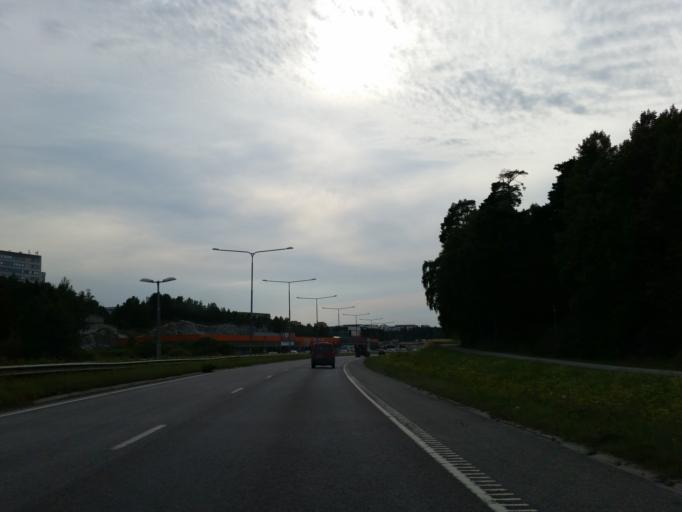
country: SE
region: Stockholm
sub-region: Sundbybergs Kommun
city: Sundbyberg
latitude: 59.3797
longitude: 17.9643
